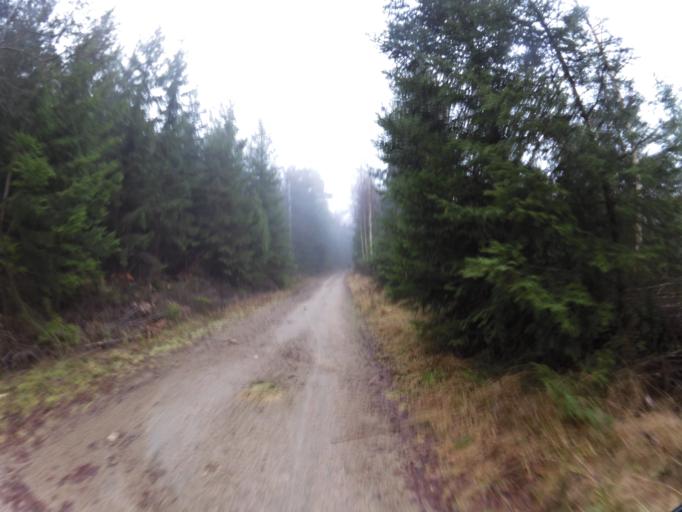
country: NO
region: Ostfold
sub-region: Fredrikstad
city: Fredrikstad
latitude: 59.2607
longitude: 10.9720
